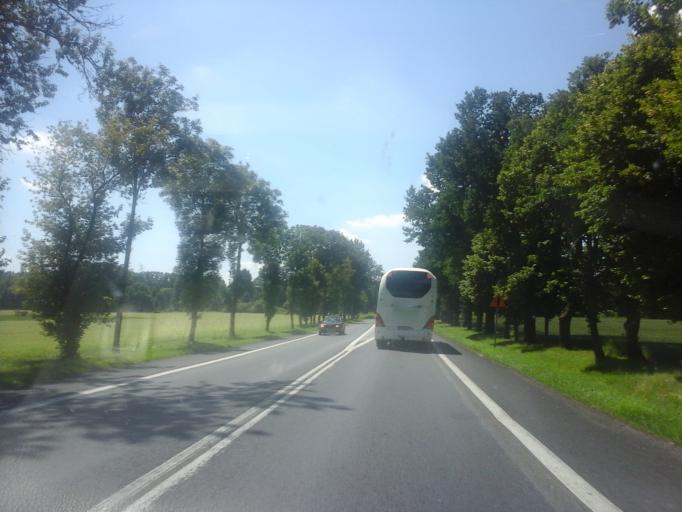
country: PL
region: West Pomeranian Voivodeship
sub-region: Powiat bialogardzki
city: Bialogard
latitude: 54.1114
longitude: 16.0009
